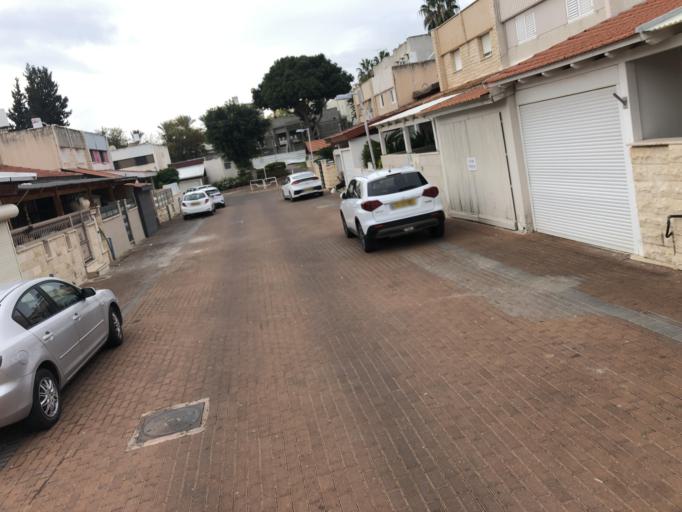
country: IL
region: Northern District
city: `Akko
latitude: 32.9319
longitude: 35.0943
